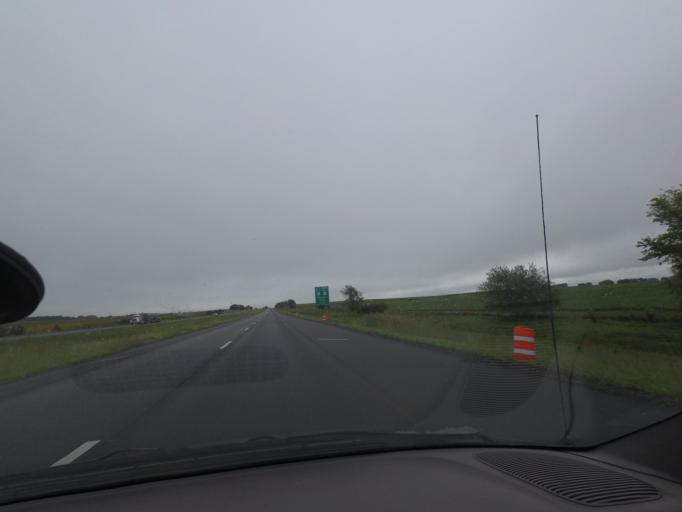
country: US
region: Illinois
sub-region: Macon County
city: Harristown
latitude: 39.8312
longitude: -89.0968
